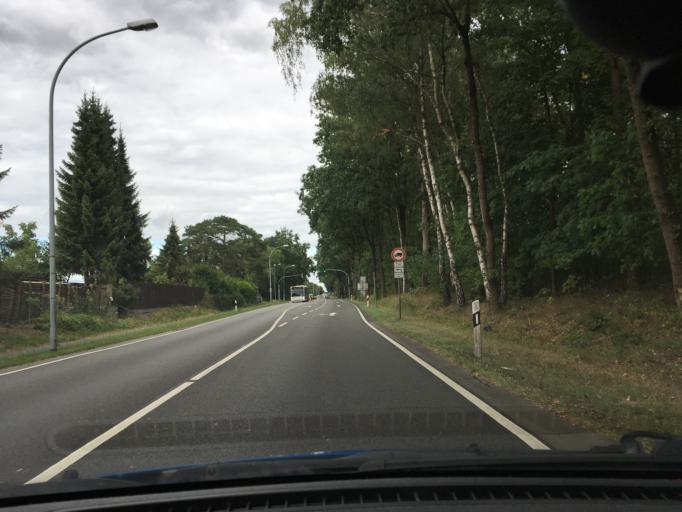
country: DE
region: Lower Saxony
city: Neu Wulmstorf
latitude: 53.4575
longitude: 9.7803
